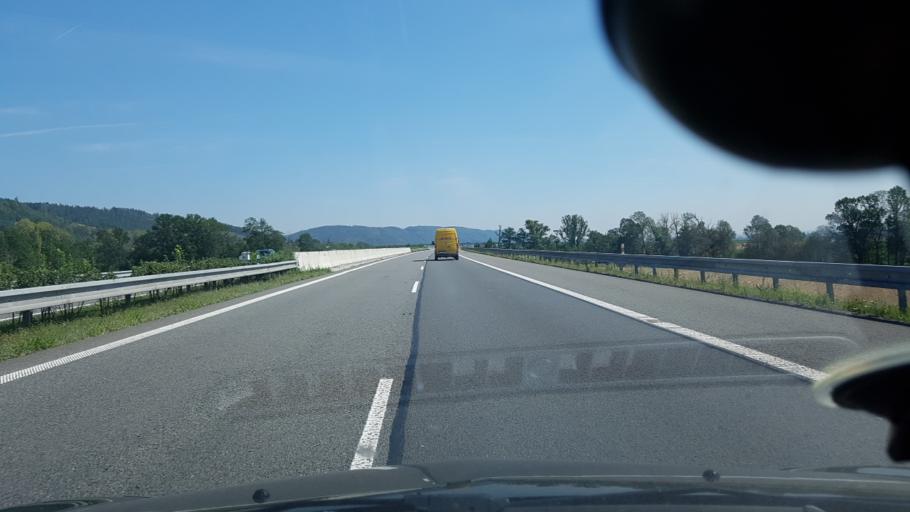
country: CZ
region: Olomoucky
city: Belotin
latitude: 49.6190
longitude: 17.8140
